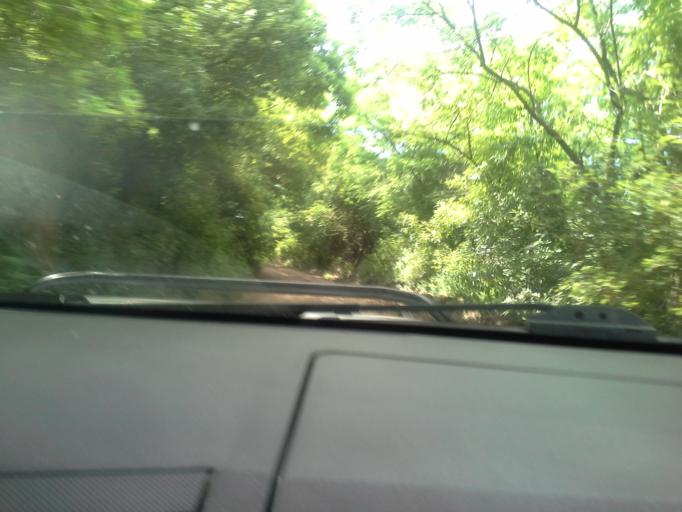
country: NI
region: Matagalpa
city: Terrabona
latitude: 12.7017
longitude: -85.9458
